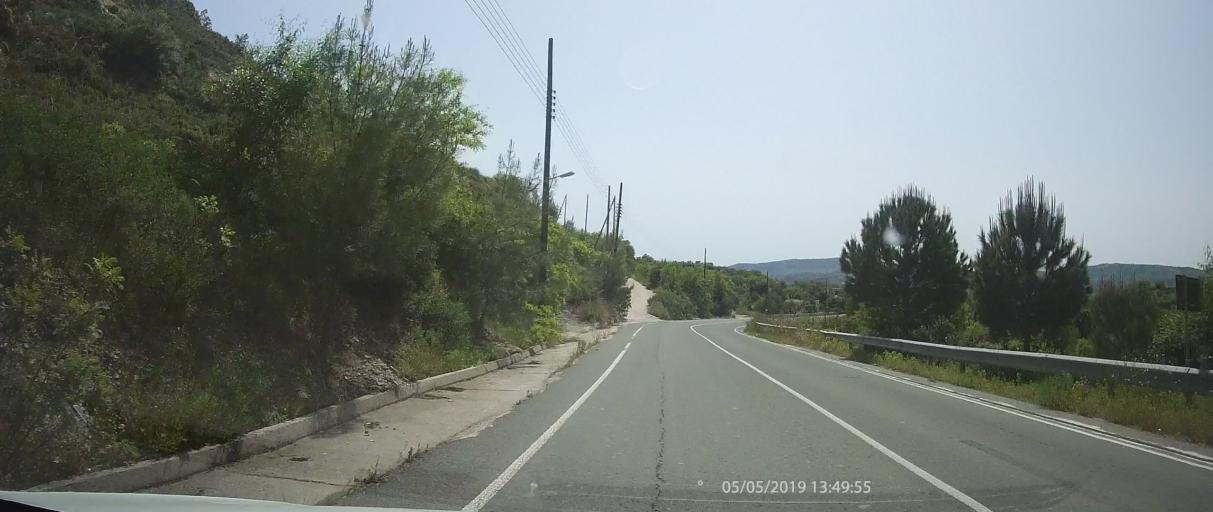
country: CY
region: Limassol
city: Pachna
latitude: 34.8453
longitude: 32.7448
